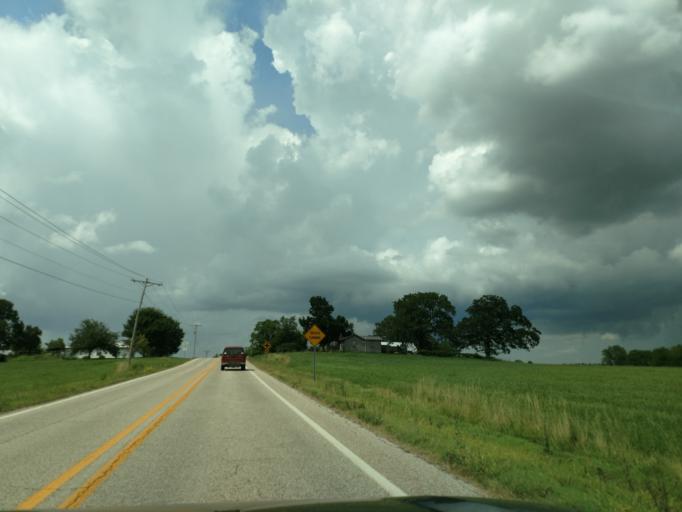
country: US
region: Arkansas
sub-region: Boone County
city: Harrison
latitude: 36.2755
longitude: -93.2345
